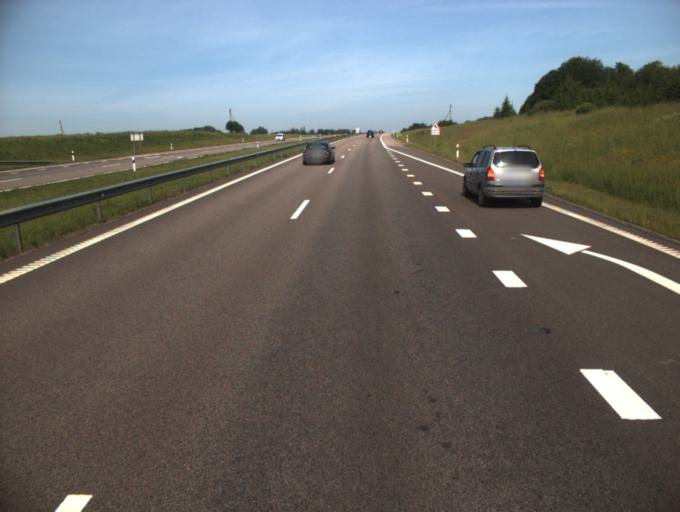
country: LT
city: Skaudvile
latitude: 55.4751
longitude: 22.6224
